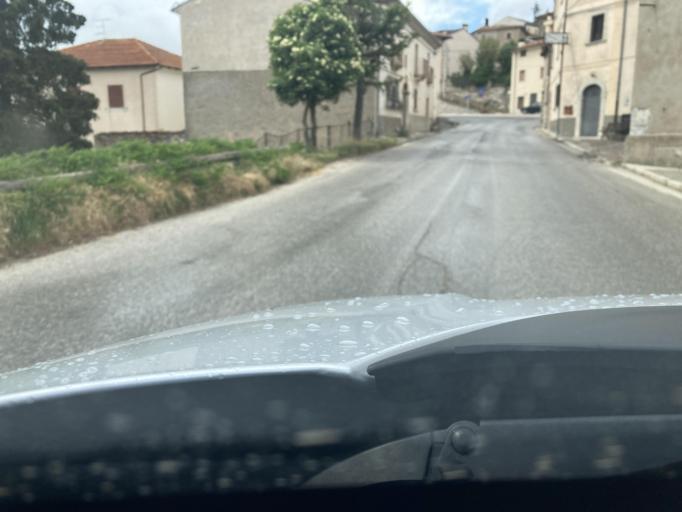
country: IT
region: Abruzzo
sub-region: Provincia dell' Aquila
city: Rocca di Mezzo
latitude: 42.2342
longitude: 13.5349
